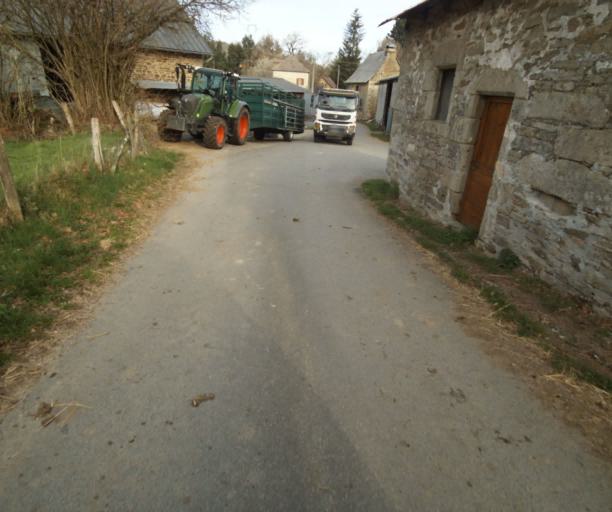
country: FR
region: Limousin
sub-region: Departement de la Correze
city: Chamboulive
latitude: 45.4454
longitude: 1.7753
